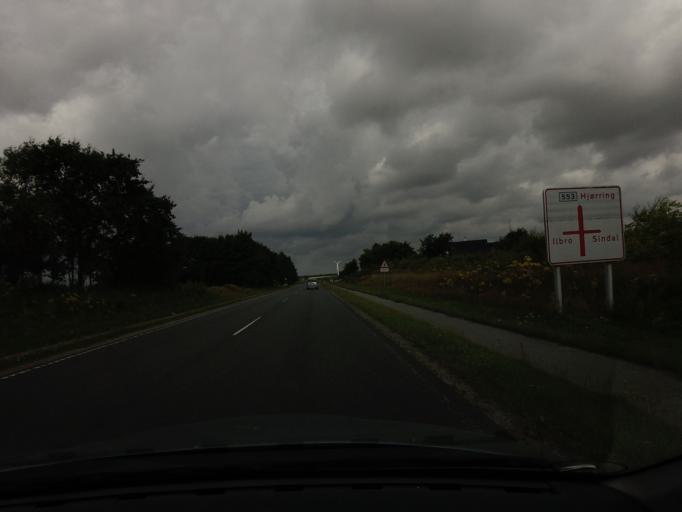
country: DK
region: North Denmark
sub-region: Hjorring Kommune
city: Tars
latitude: 57.4174
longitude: 10.0588
